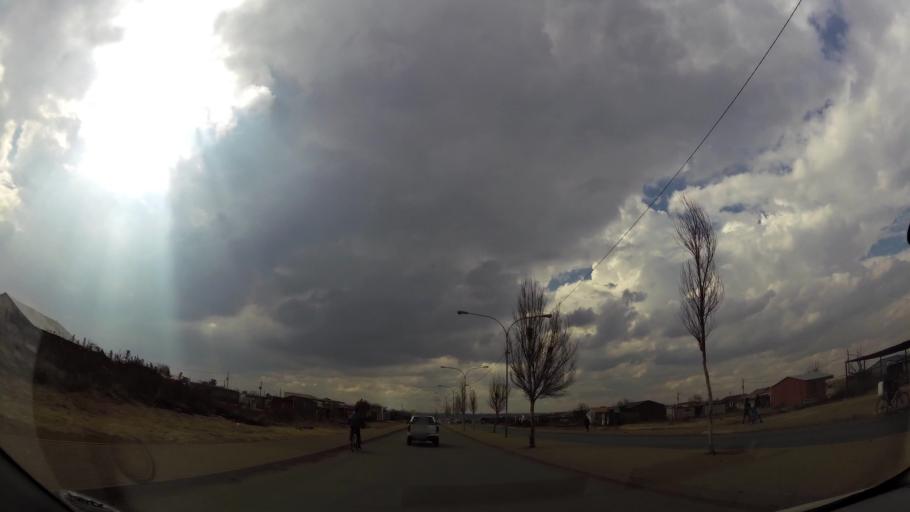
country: ZA
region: Gauteng
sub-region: Ekurhuleni Metropolitan Municipality
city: Germiston
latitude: -26.3949
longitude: 28.1587
